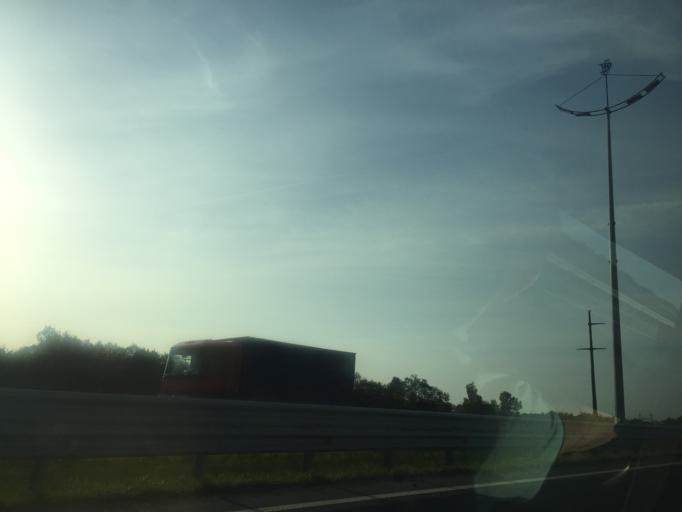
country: RU
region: Kaliningrad
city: Maloye Isakovo
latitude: 54.7568
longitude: 20.5819
